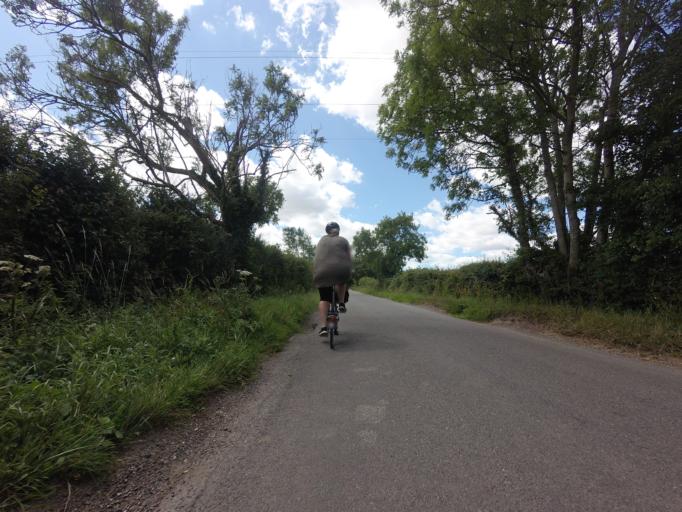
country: GB
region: England
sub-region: East Sussex
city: Ringmer
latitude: 50.8658
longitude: 0.1403
